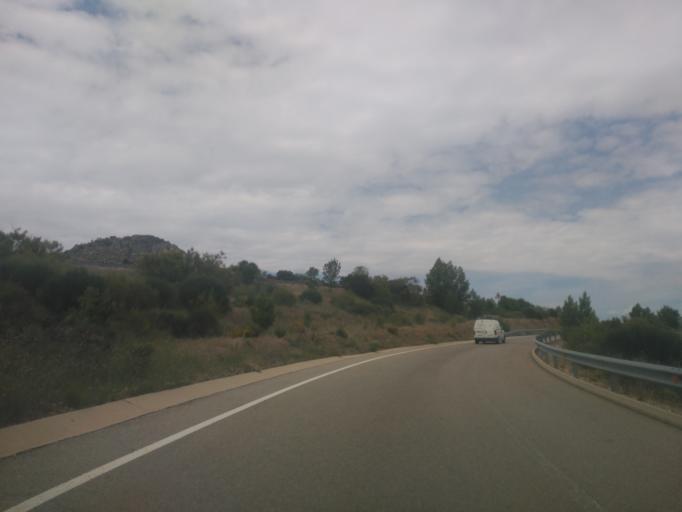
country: ES
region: Castille and Leon
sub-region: Provincia de Salamanca
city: Vallejera de Riofrio
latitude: 40.3979
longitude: -5.7378
